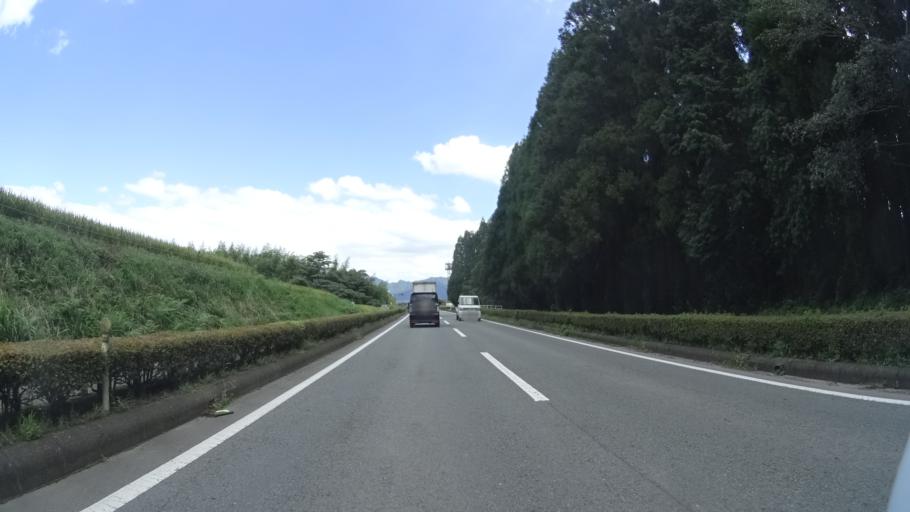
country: JP
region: Kumamoto
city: Aso
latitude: 32.8305
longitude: 131.0868
